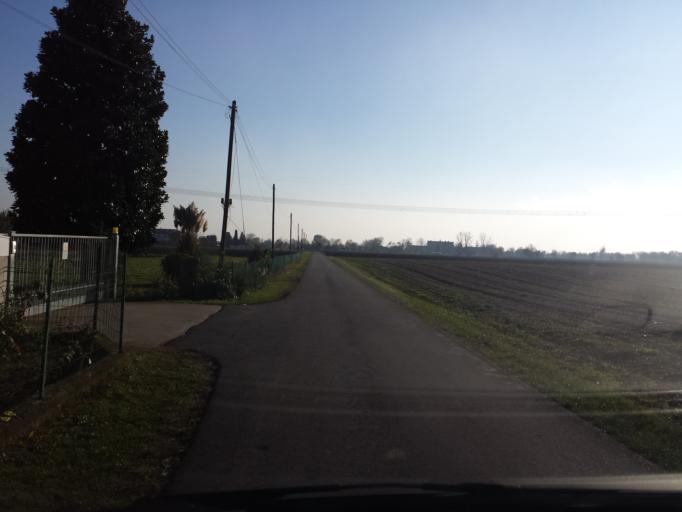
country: IT
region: Veneto
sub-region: Provincia di Vicenza
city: Sandrigo
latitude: 45.6801
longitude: 11.5842
